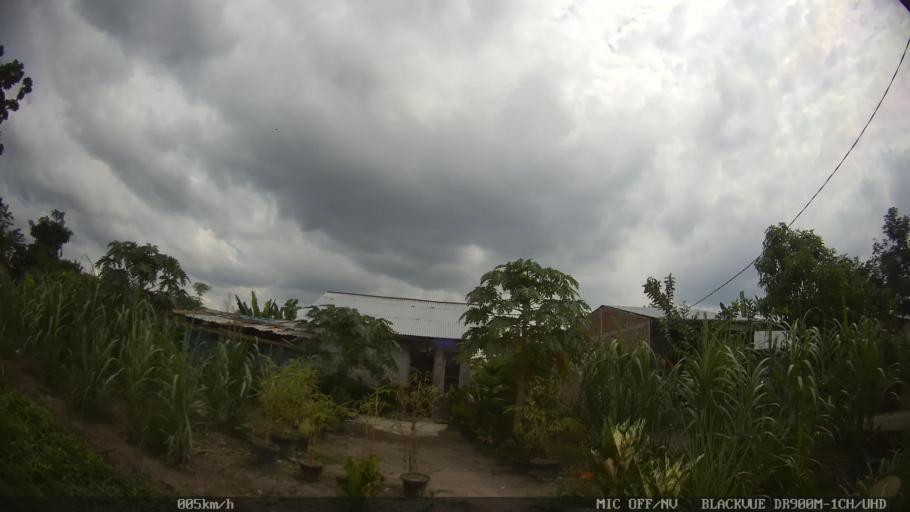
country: ID
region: North Sumatra
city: Sunggal
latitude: 3.6241
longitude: 98.5975
